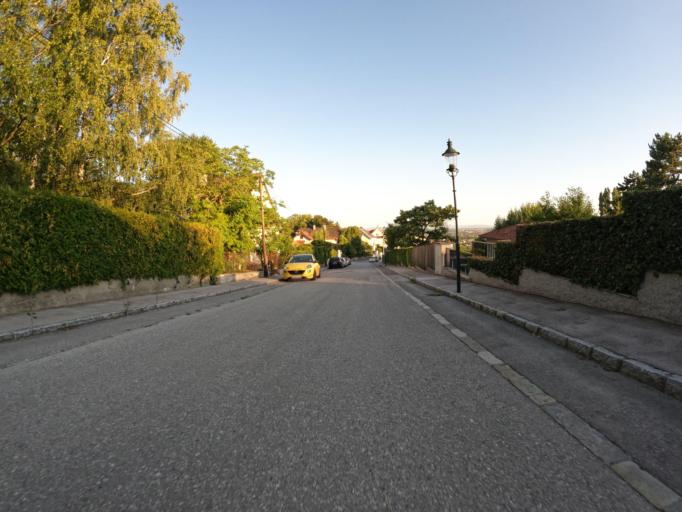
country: AT
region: Lower Austria
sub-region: Politischer Bezirk Baden
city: Baden
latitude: 48.0154
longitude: 16.2248
